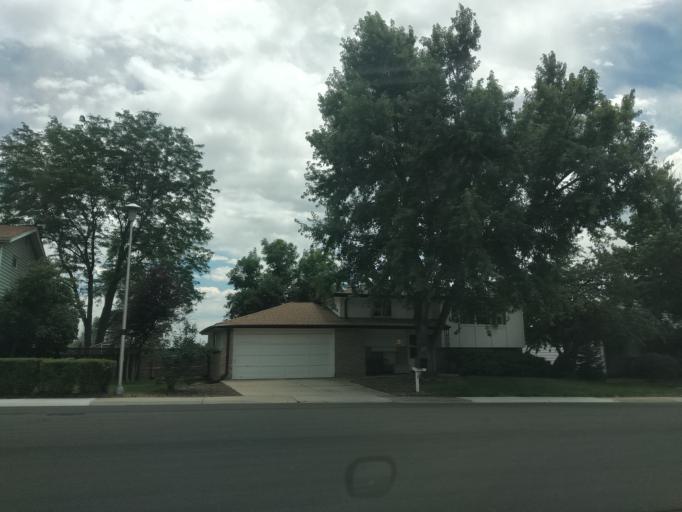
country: US
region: Colorado
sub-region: Jefferson County
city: Lakewood
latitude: 39.6726
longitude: -105.0985
